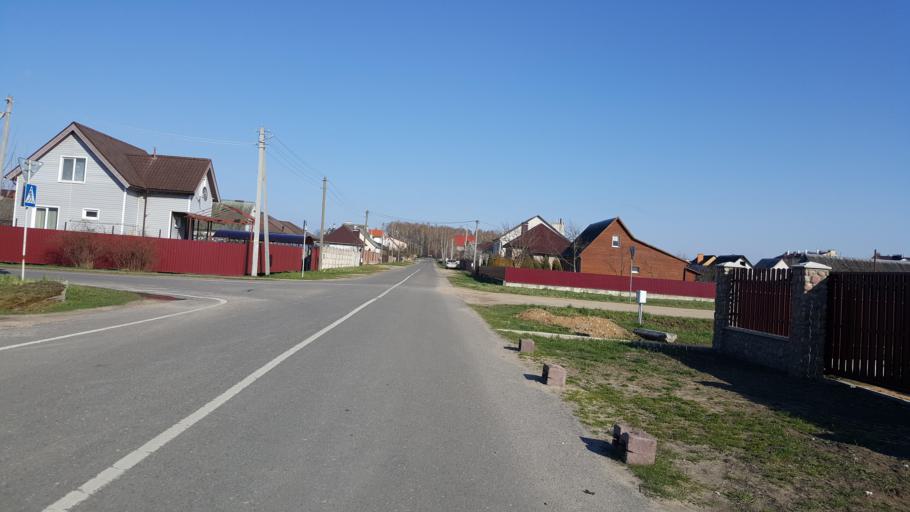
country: BY
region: Brest
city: Kamyanyets
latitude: 52.3929
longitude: 23.8125
